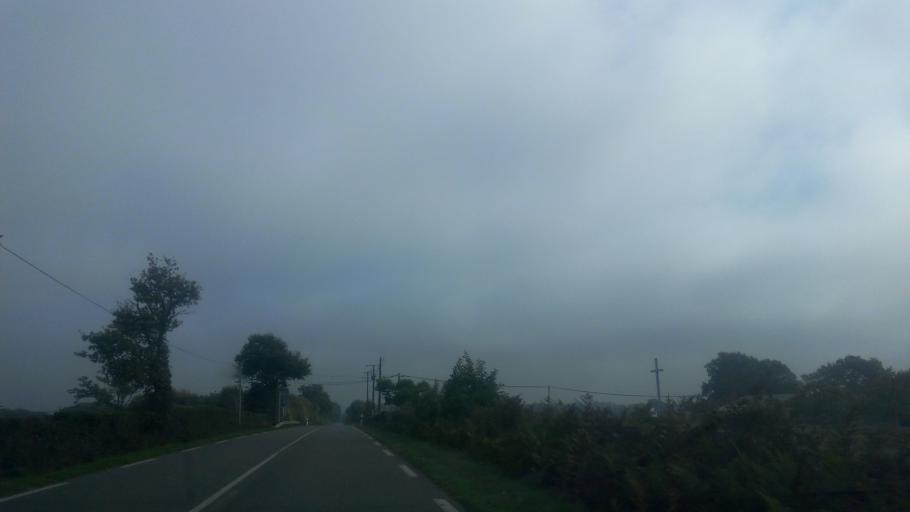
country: FR
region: Pays de la Loire
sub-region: Departement de la Loire-Atlantique
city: Avessac
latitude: 47.6377
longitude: -1.9782
